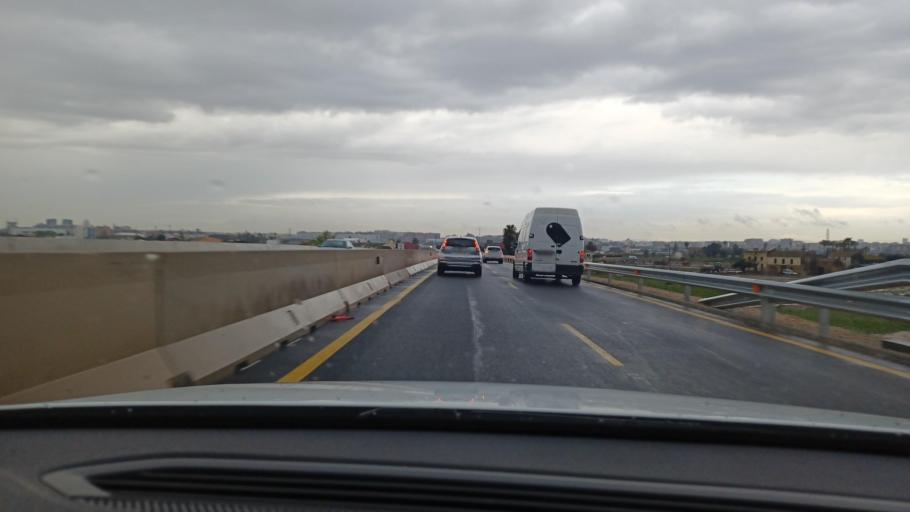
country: ES
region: Valencia
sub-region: Provincia de Valencia
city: Alboraya
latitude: 39.4947
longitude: -0.3298
